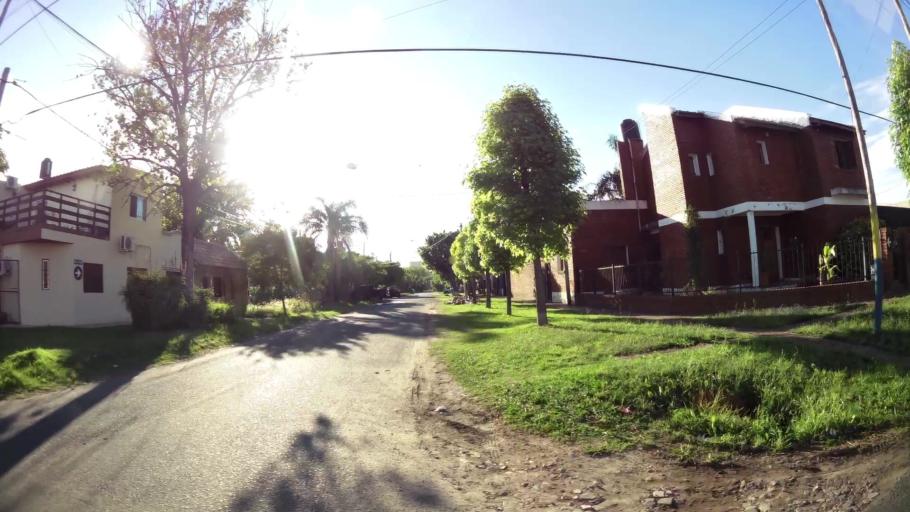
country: AR
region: Santa Fe
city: Gobernador Galvez
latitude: -32.9905
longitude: -60.6765
